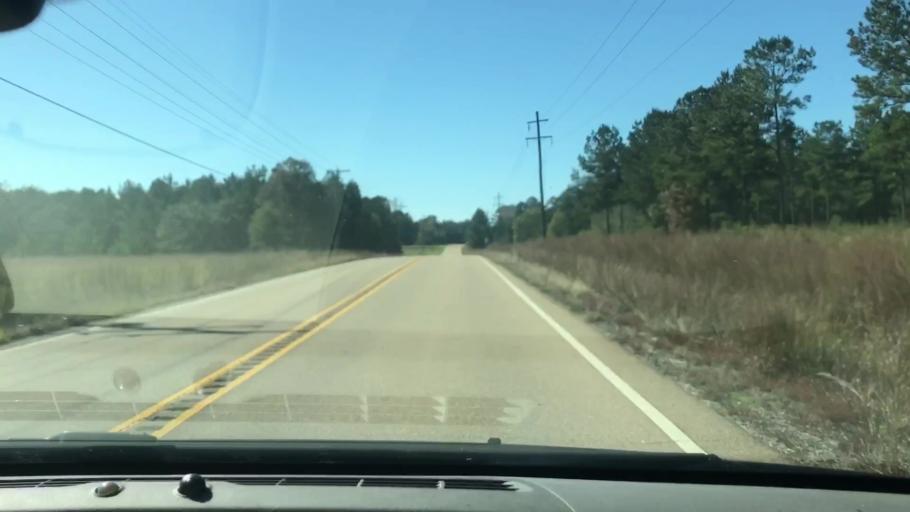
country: US
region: Louisiana
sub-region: Saint Tammany Parish
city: Abita Springs
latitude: 30.5207
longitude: -89.9348
